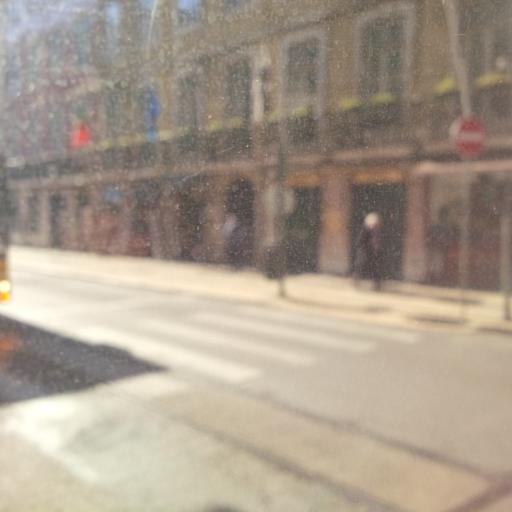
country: PT
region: Lisbon
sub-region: Lisbon
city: Lisbon
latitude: 38.7097
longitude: -9.1363
